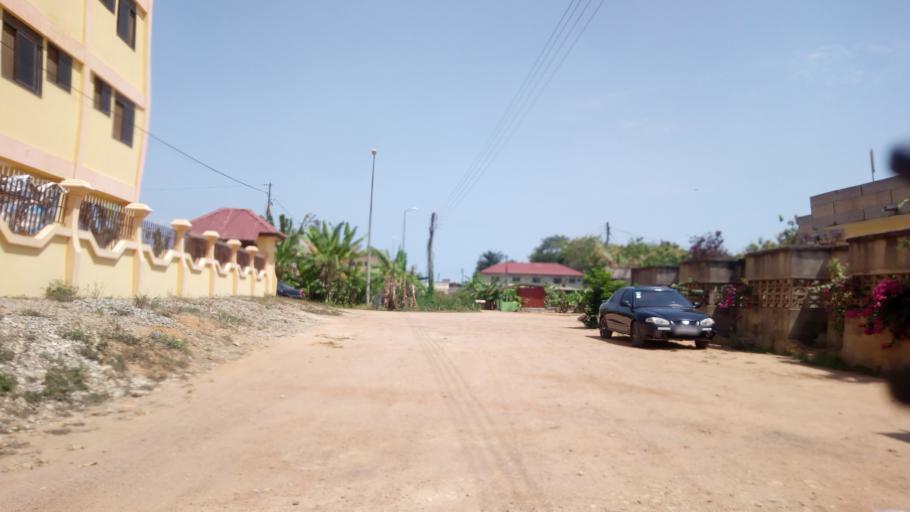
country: GH
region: Central
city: Cape Coast
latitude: 5.1324
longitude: -1.2824
